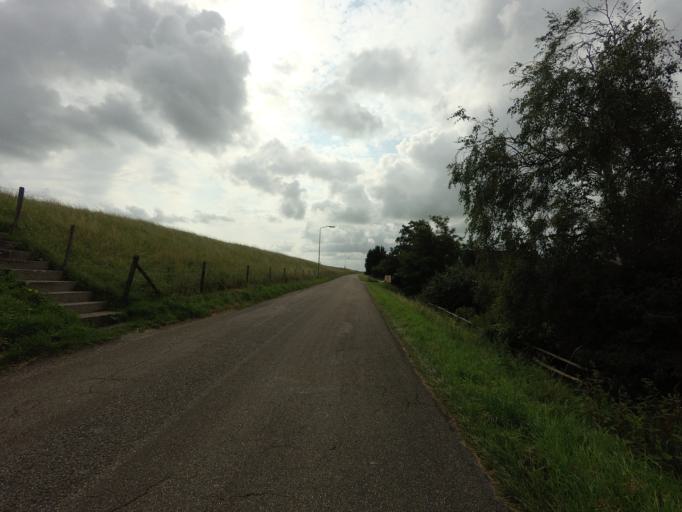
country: NL
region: North Holland
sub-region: Gemeente Hoorn
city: Hoorn
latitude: 52.6189
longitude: 5.0167
